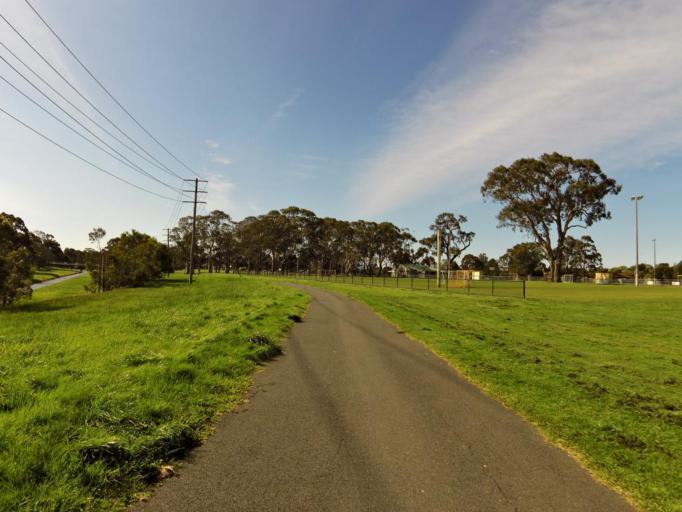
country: AU
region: Victoria
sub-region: Casey
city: Doveton
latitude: -37.9898
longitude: 145.2295
